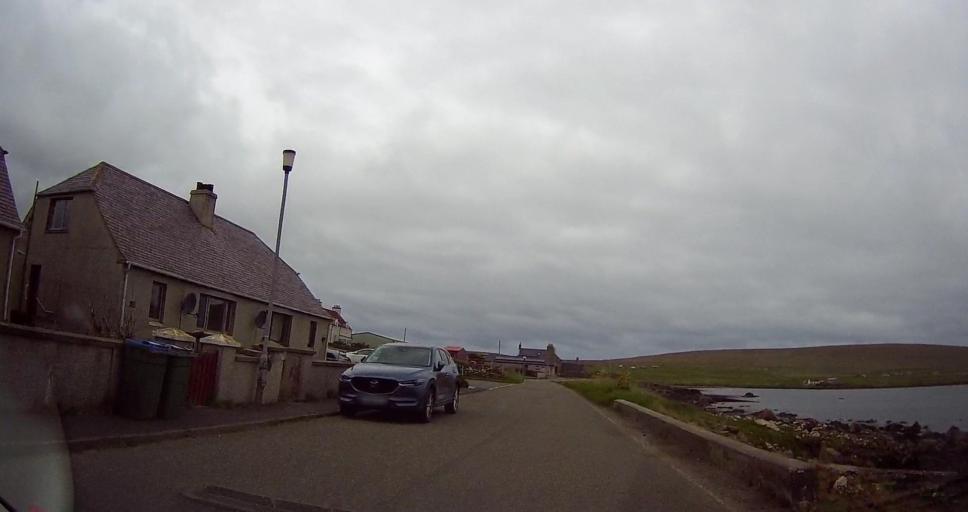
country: GB
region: Scotland
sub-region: Shetland Islands
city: Shetland
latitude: 60.7882
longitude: -0.8301
